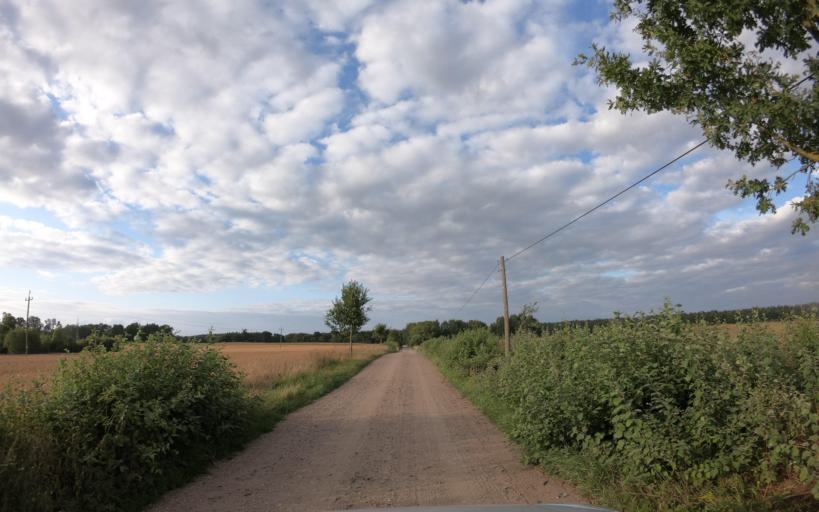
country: PL
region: West Pomeranian Voivodeship
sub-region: Powiat drawski
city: Czaplinek
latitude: 53.5307
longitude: 16.1550
